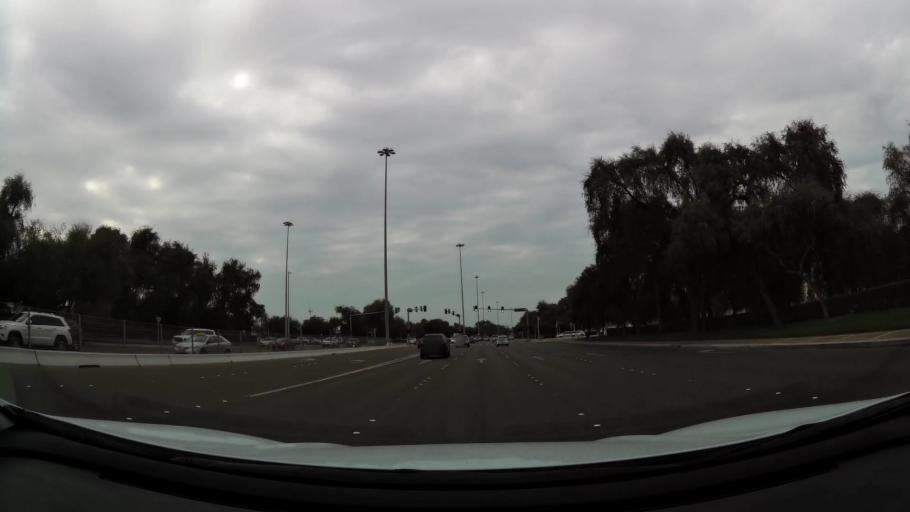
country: AE
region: Abu Dhabi
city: Abu Dhabi
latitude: 24.4361
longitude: 54.4056
